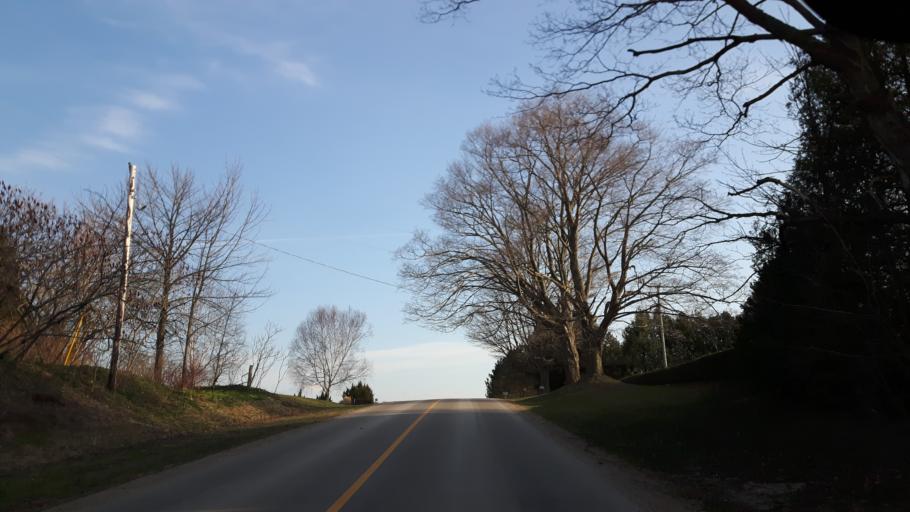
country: CA
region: Ontario
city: Goderich
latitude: 43.6565
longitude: -81.6643
